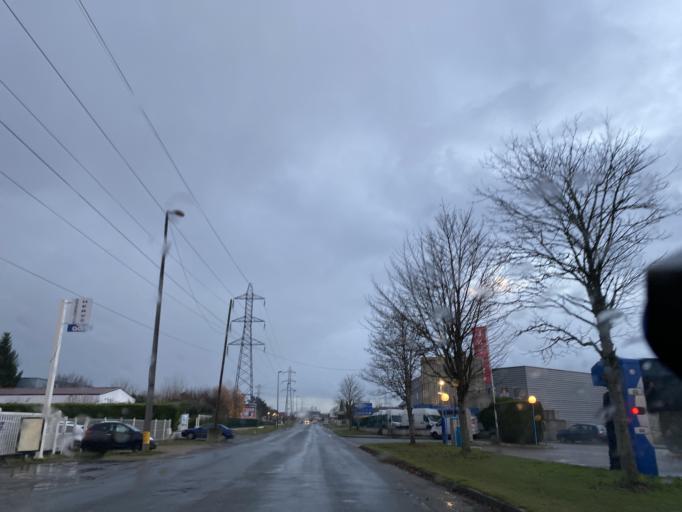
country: FR
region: Haute-Normandie
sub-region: Departement de l'Eure
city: Gravigny
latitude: 49.0262
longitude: 1.1803
